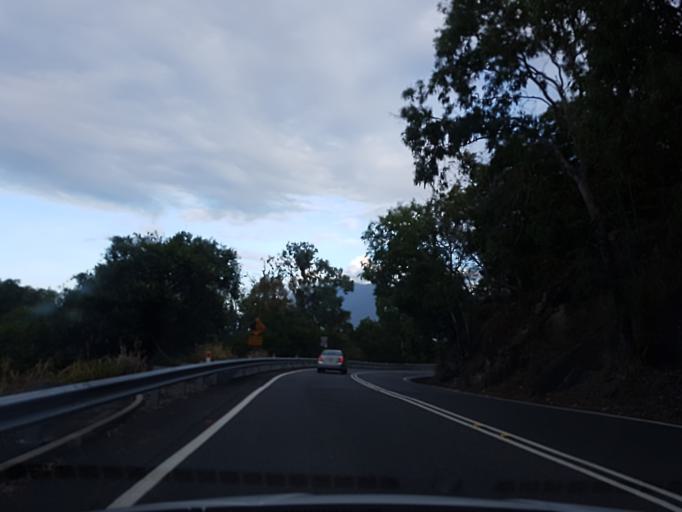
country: AU
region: Queensland
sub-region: Cairns
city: Palm Cove
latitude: -16.6480
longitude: 145.5652
